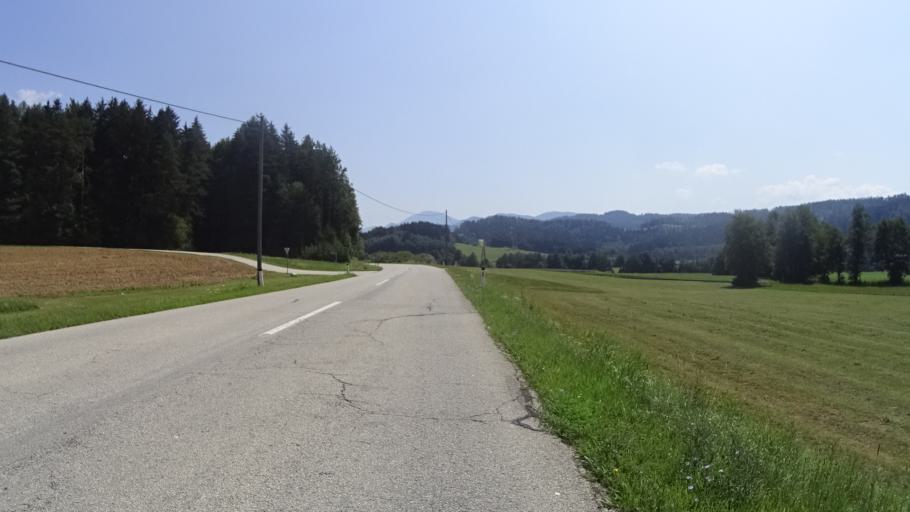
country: AT
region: Carinthia
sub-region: Politischer Bezirk Volkermarkt
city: Bleiburg/Pliberk
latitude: 46.5685
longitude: 14.8307
